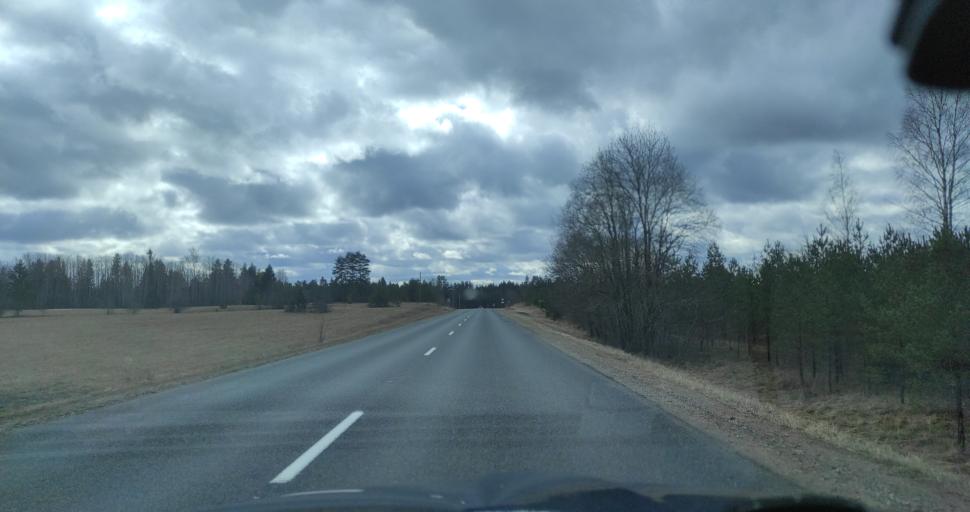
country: LV
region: Talsu Rajons
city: Stende
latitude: 57.0878
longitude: 22.4754
